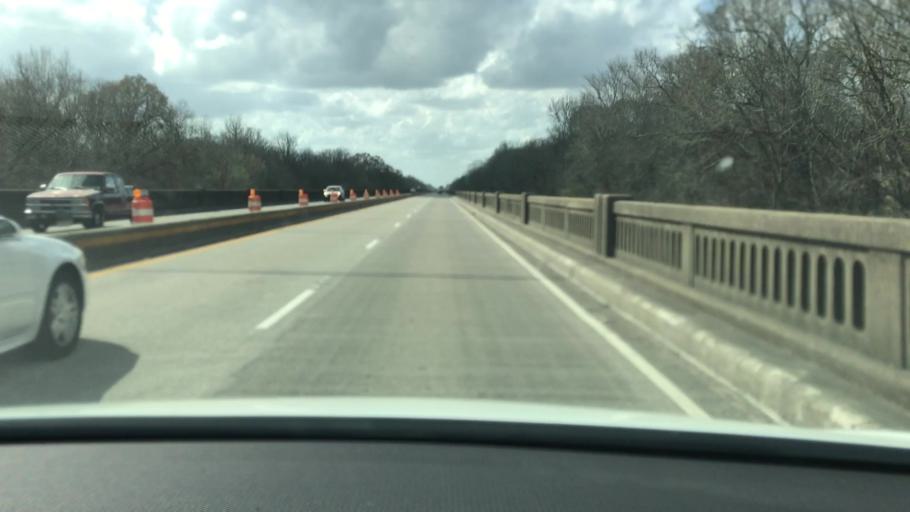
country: US
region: Louisiana
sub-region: Saint Landry Parish
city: Krotz Springs
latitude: 30.5558
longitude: -91.6722
